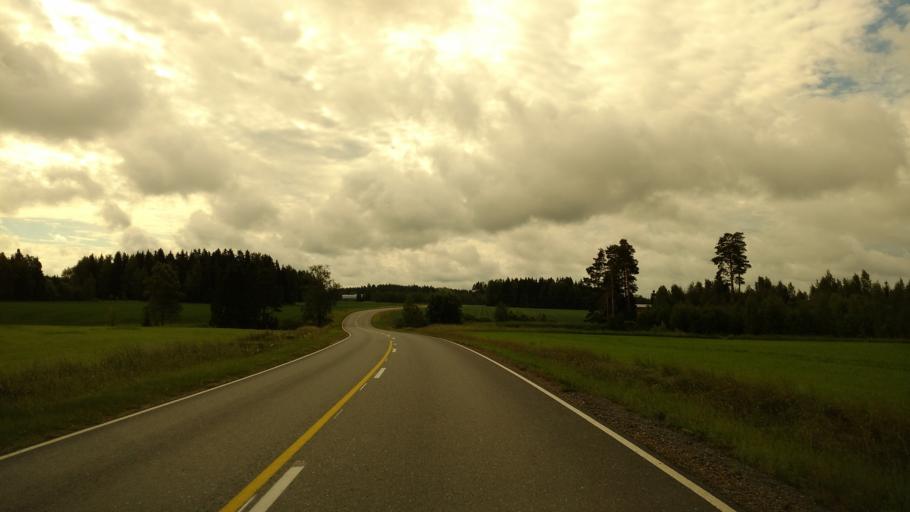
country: FI
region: Varsinais-Suomi
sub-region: Loimaa
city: Koski Tl
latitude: 60.5924
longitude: 23.1306
